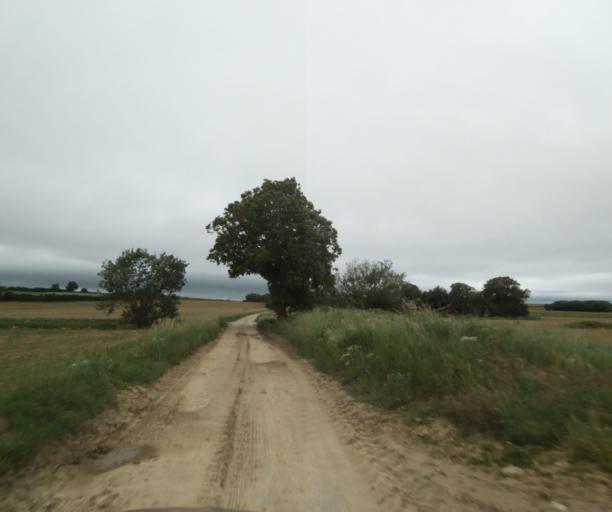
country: FR
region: Rhone-Alpes
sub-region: Departement de l'Ain
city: Miribel
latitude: 45.8426
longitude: 4.9439
